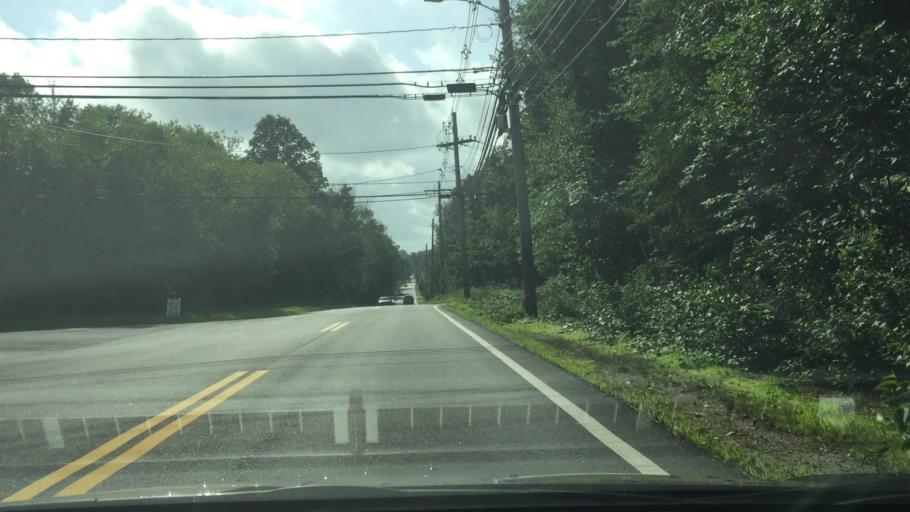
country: US
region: Massachusetts
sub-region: Middlesex County
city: Stow
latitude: 42.4795
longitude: -71.4952
